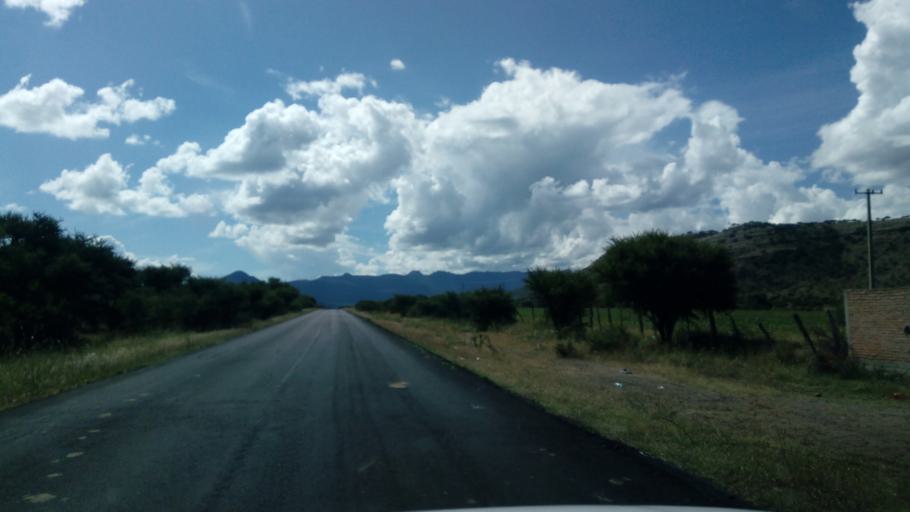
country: MX
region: Durango
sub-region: Durango
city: Jose Refugio Salcido
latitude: 23.8209
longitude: -104.4829
